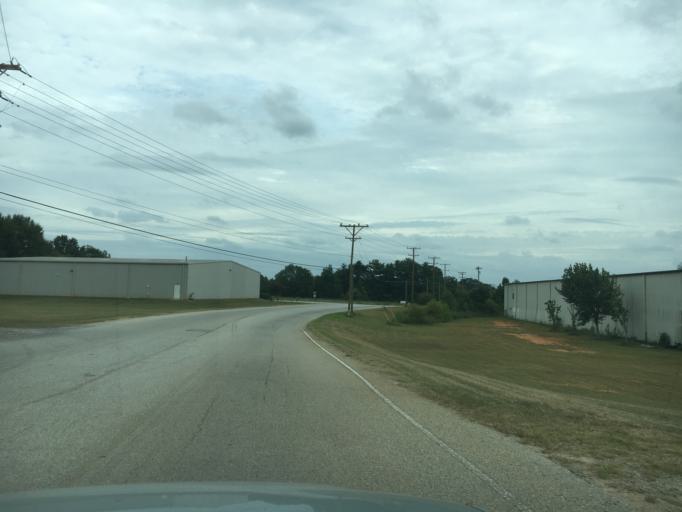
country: US
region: South Carolina
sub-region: Spartanburg County
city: Duncan
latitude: 34.9056
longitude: -82.1589
